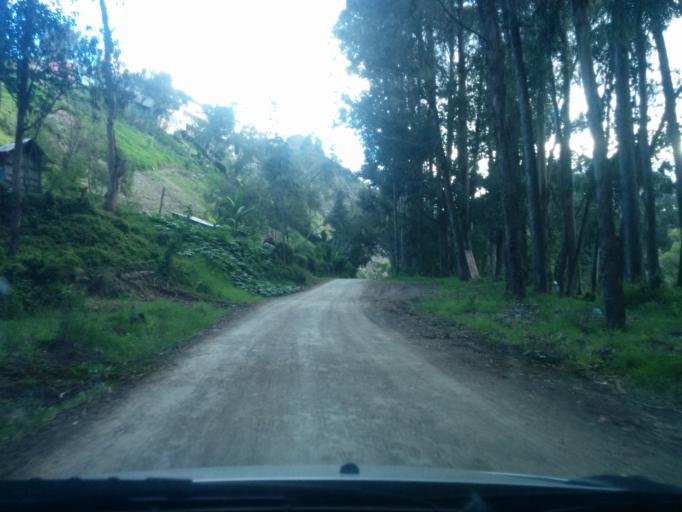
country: EC
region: Azuay
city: Cuenca
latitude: -2.8855
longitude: -78.9503
